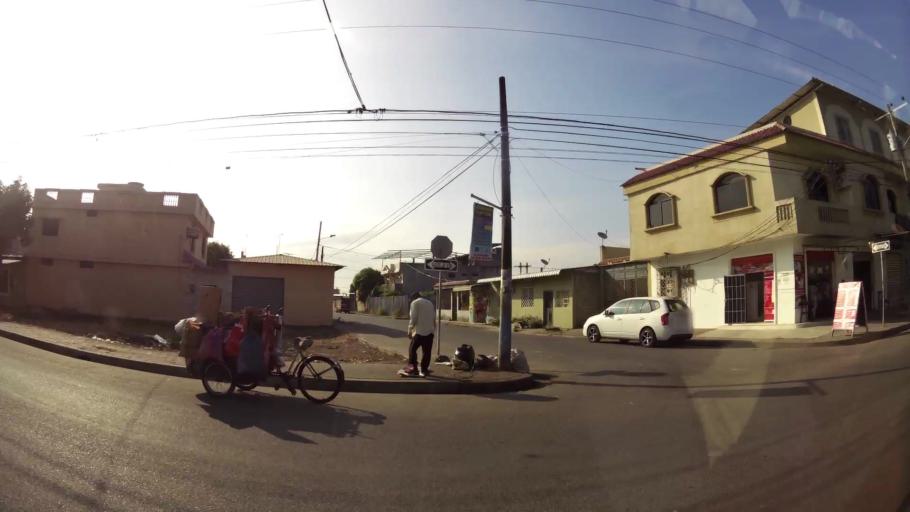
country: EC
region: Guayas
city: Eloy Alfaro
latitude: -2.1826
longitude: -79.8457
